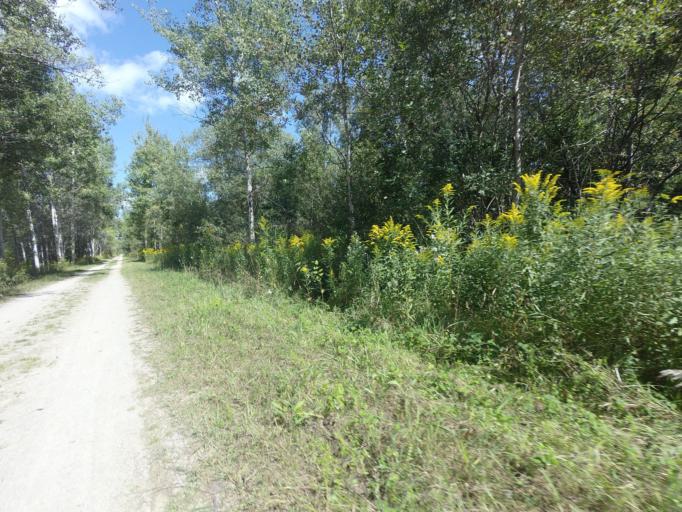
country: CA
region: Ontario
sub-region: Wellington County
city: Guelph
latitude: 43.7554
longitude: -80.3216
